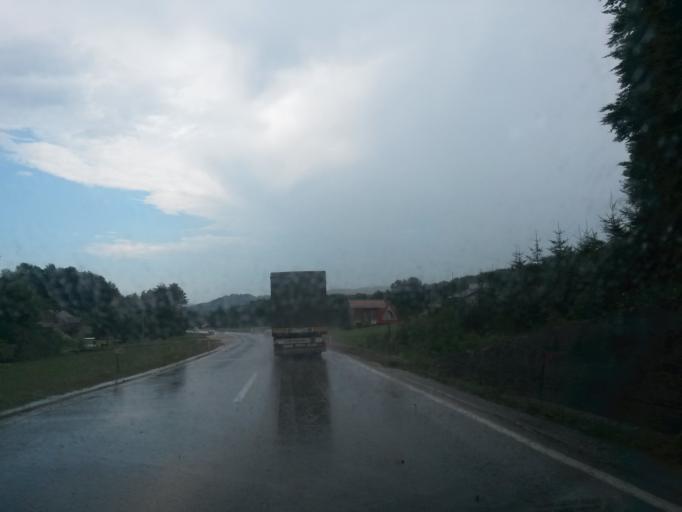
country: BA
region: Federation of Bosnia and Herzegovina
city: Lijesnica
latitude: 44.4699
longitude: 18.0679
